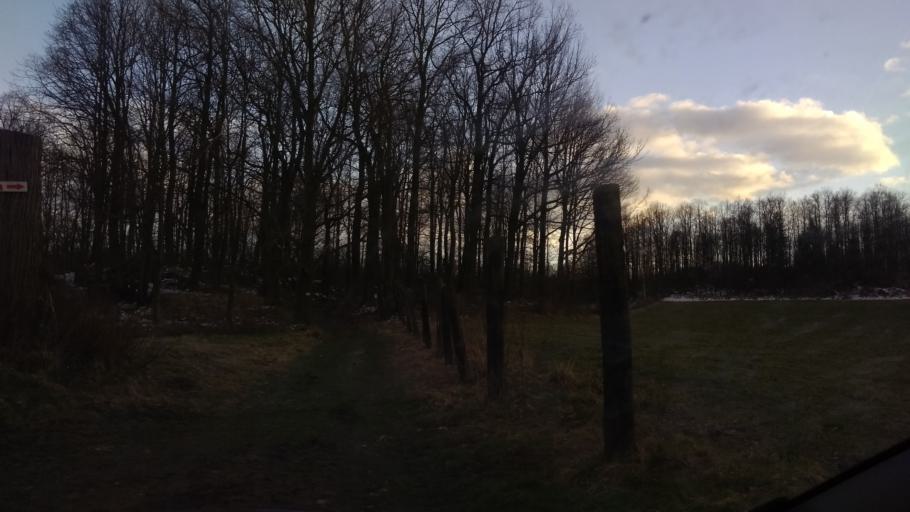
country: PL
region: Lower Silesian Voivodeship
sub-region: Powiat jeleniogorski
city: Sosnowka
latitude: 50.8494
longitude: 15.7318
